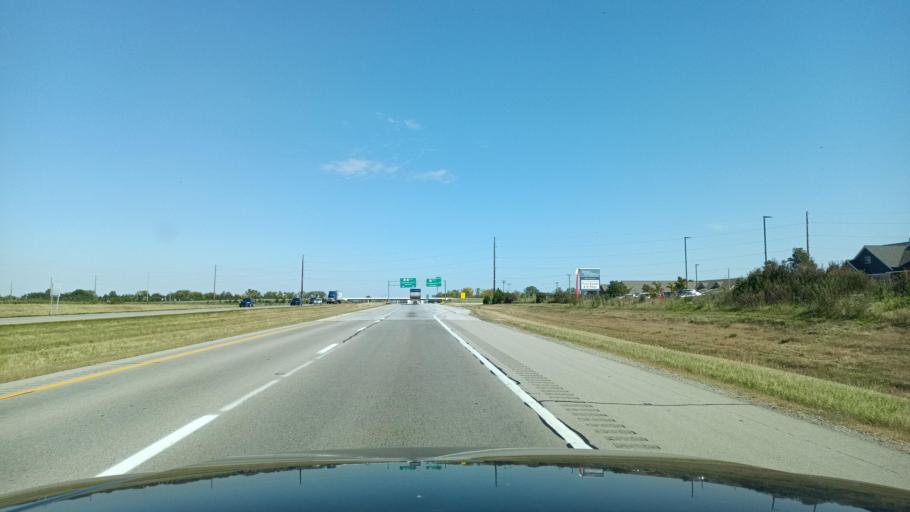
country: US
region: Ohio
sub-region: Henry County
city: Napoleon
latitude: 41.3922
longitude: -84.1535
